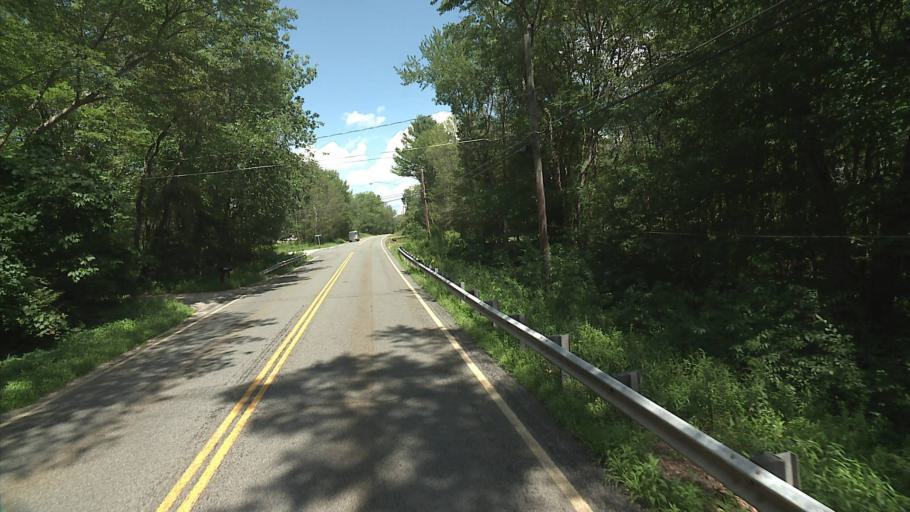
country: US
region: Connecticut
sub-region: Tolland County
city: Mansfield City
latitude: 41.7865
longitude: -72.1795
